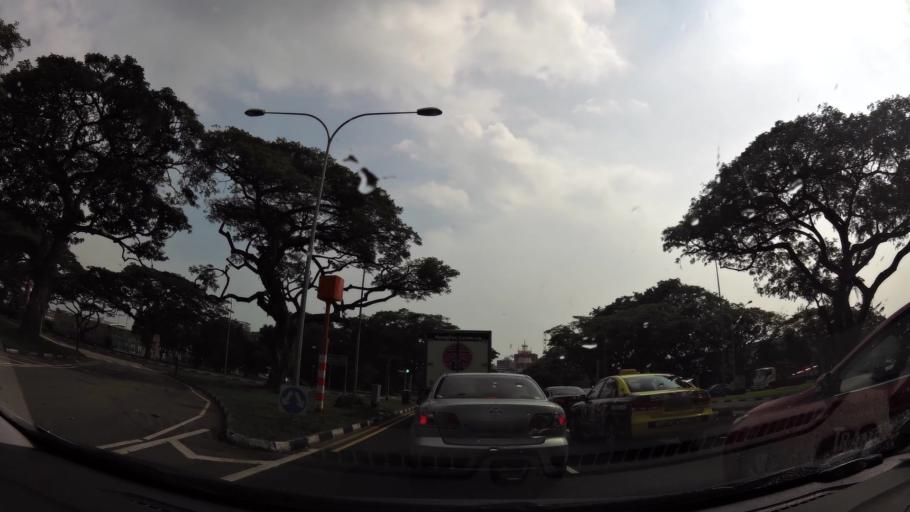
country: SG
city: Singapore
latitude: 1.3193
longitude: 103.9328
